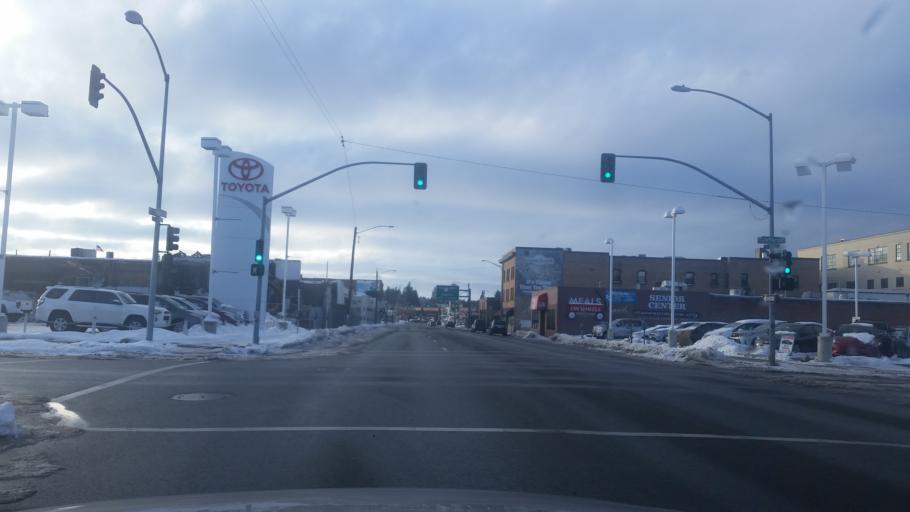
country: US
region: Washington
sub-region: Spokane County
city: Spokane
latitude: 47.6545
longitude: -117.4294
